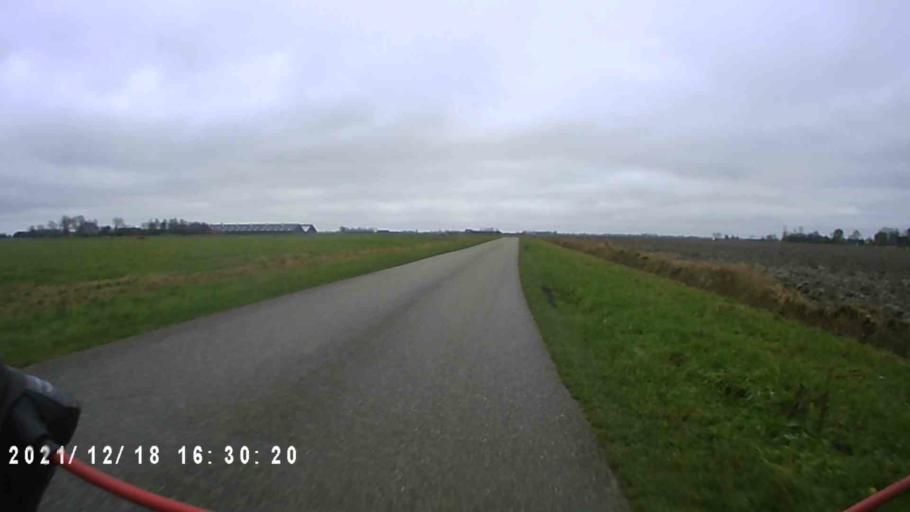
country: NL
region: Friesland
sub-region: Gemeente Dongeradeel
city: Dokkum
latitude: 53.3603
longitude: 6.0385
